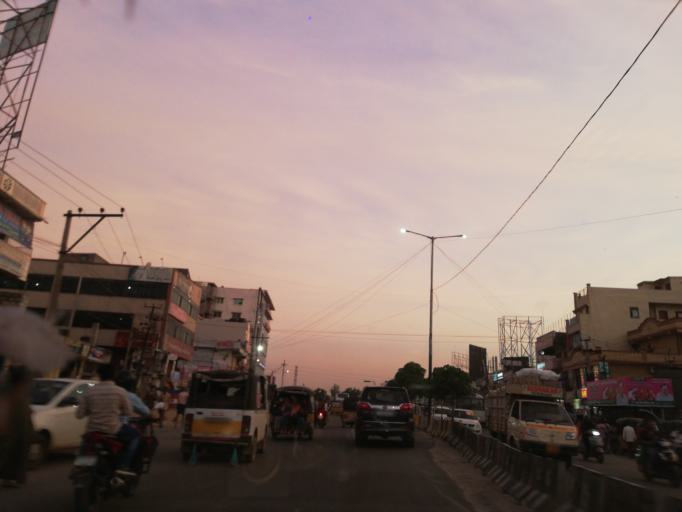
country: IN
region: Telangana
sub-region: Rangareddi
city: Kukatpalli
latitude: 17.4982
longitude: 78.3618
